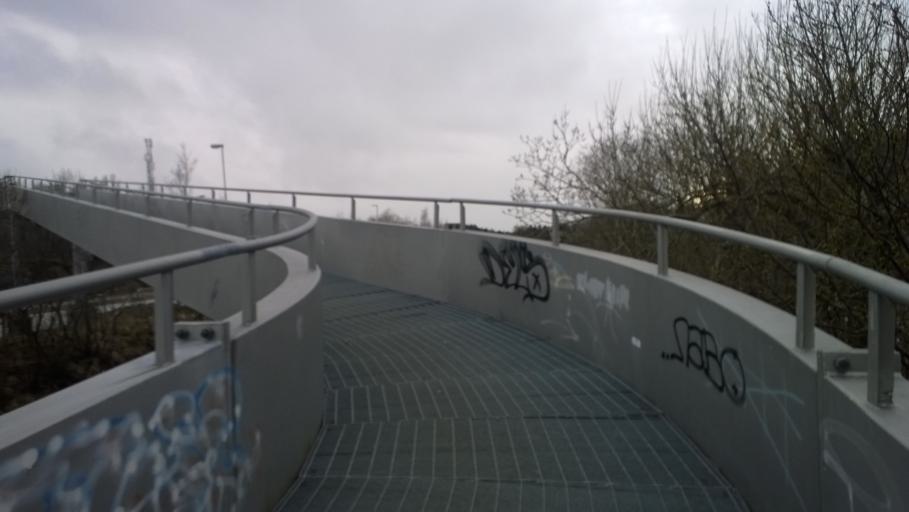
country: NO
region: Nordland
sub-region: Bodo
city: Lopsmarka
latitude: 67.2784
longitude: 14.4910
